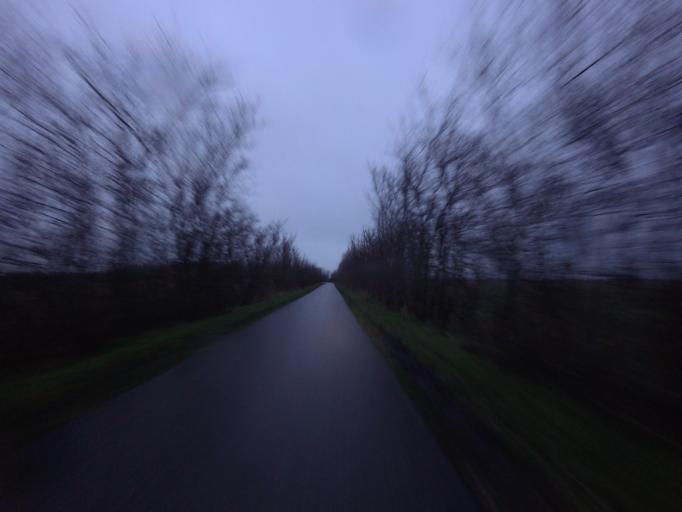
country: NL
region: North Holland
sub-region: Gemeente Texel
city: Den Burg
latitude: 53.0666
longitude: 4.7966
